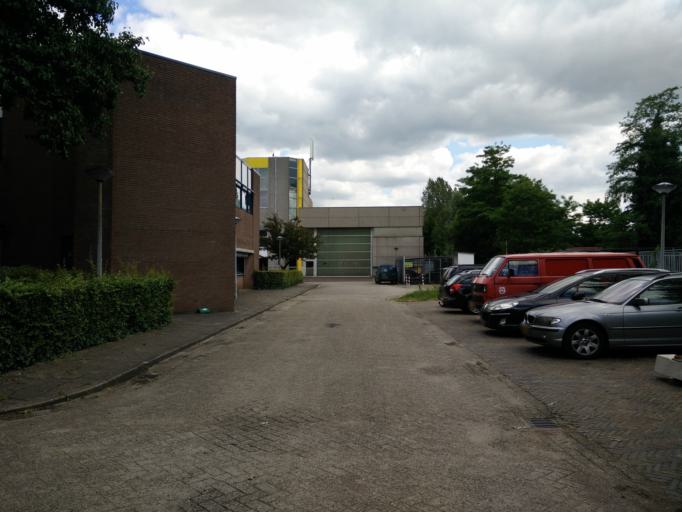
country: NL
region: Utrecht
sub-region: Gemeente Utrecht
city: Utrecht
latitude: 52.0994
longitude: 5.0967
